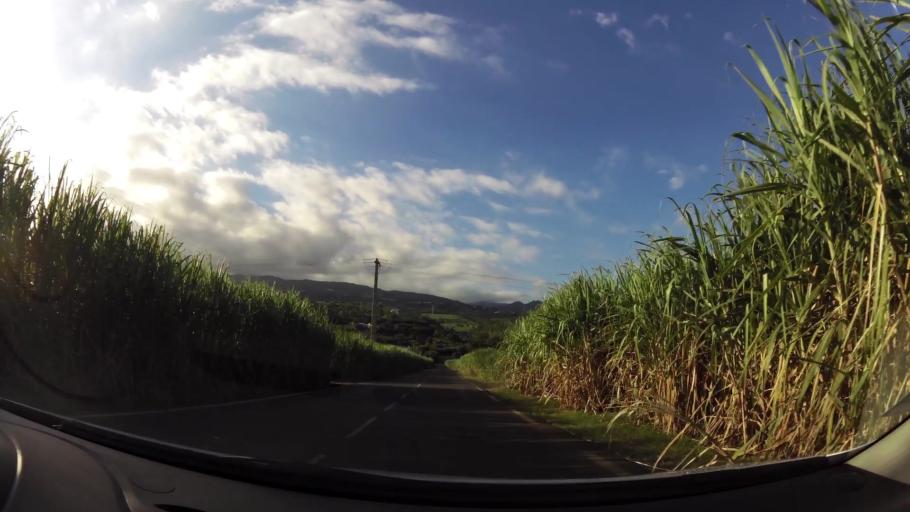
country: RE
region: Reunion
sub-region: Reunion
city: Saint-Louis
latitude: -21.2678
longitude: 55.3789
